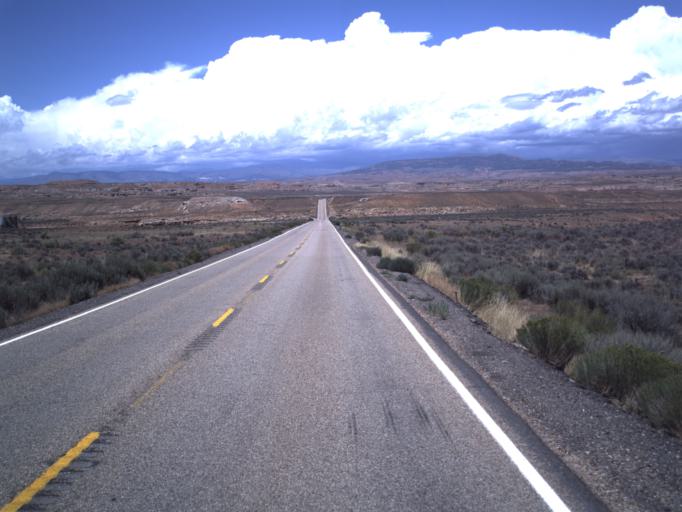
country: US
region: Utah
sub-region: Uintah County
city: Maeser
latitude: 40.3002
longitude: -109.6880
